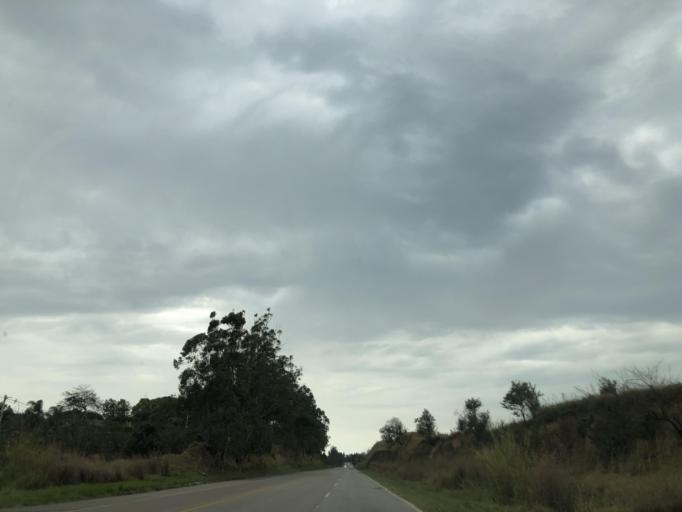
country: BR
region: Sao Paulo
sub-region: Salto De Pirapora
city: Salto de Pirapora
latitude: -23.7017
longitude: -47.6225
